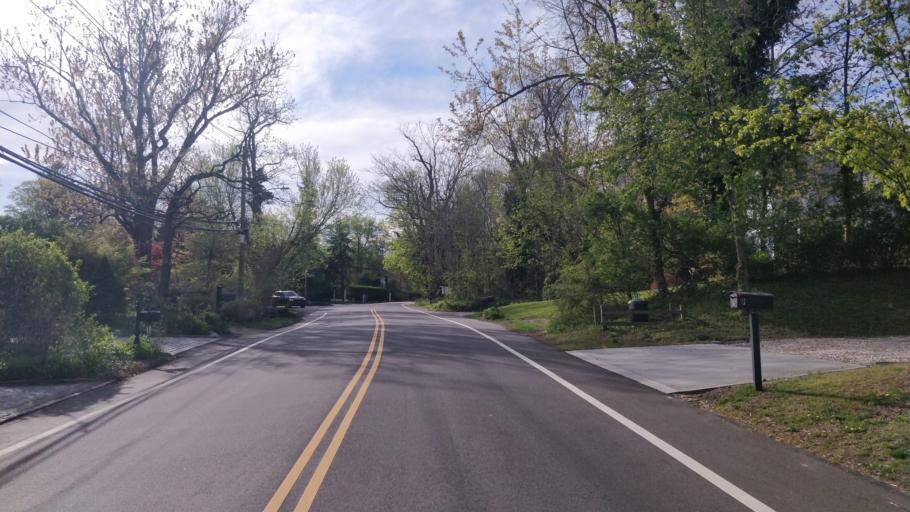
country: US
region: New York
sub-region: Suffolk County
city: East Setauket
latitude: 40.9455
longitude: -73.1182
